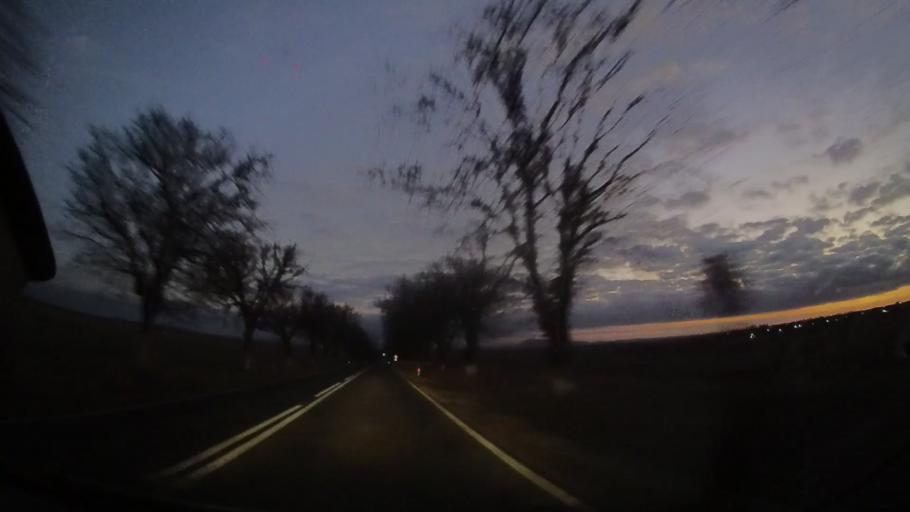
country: RO
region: Tulcea
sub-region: Comuna Frecatei
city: Cataloi
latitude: 45.0934
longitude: 28.7414
